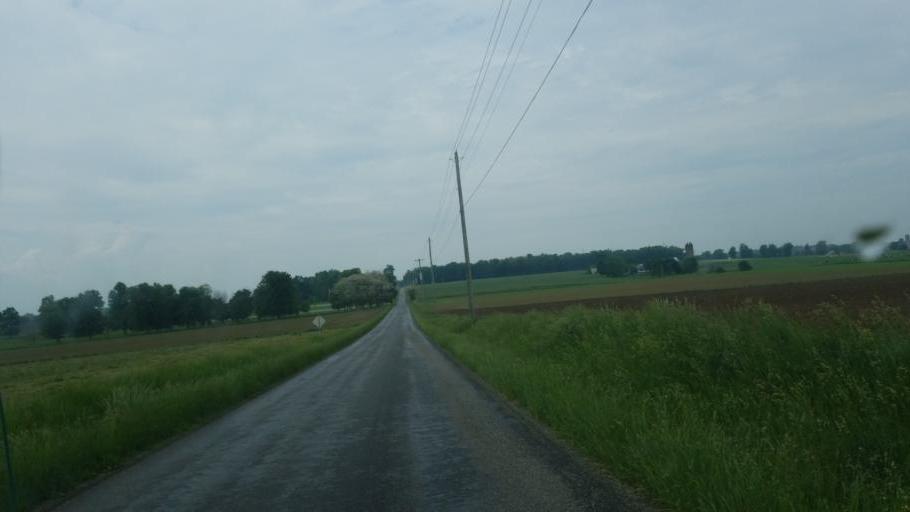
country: US
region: Ohio
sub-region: Wayne County
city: Dalton
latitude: 40.8145
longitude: -81.7268
